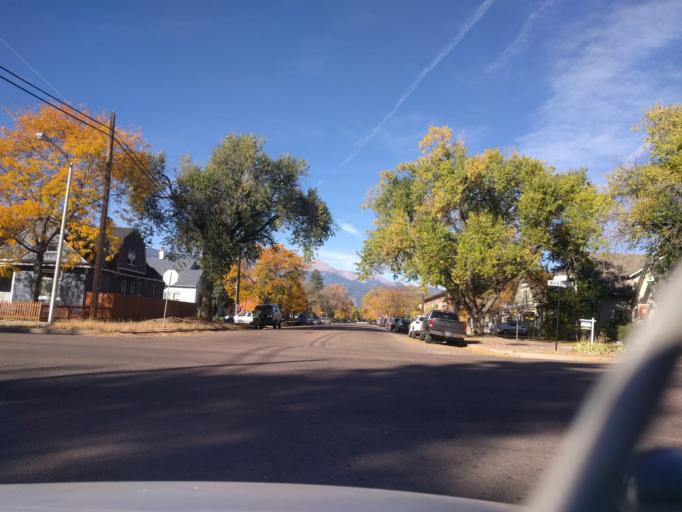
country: US
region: Colorado
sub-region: El Paso County
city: Colorado Springs
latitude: 38.8519
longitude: -104.8188
